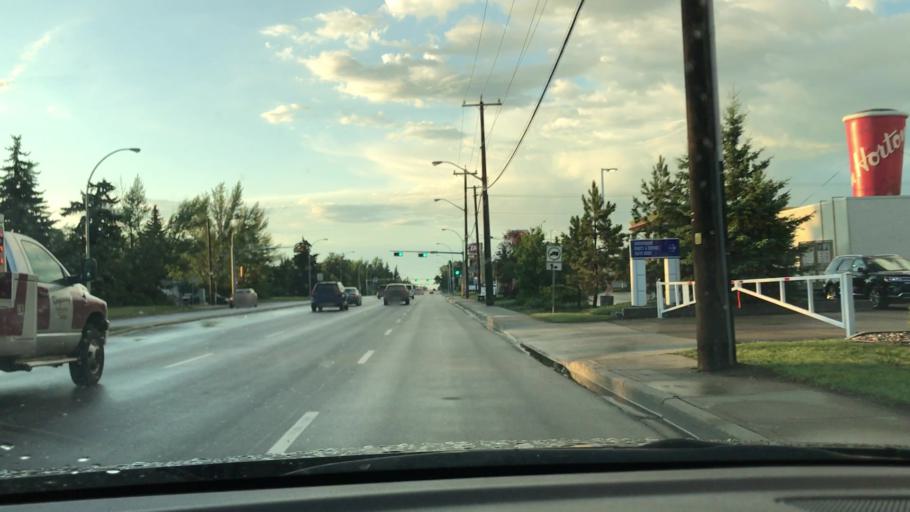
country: CA
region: Alberta
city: Edmonton
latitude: 53.5113
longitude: -113.4427
